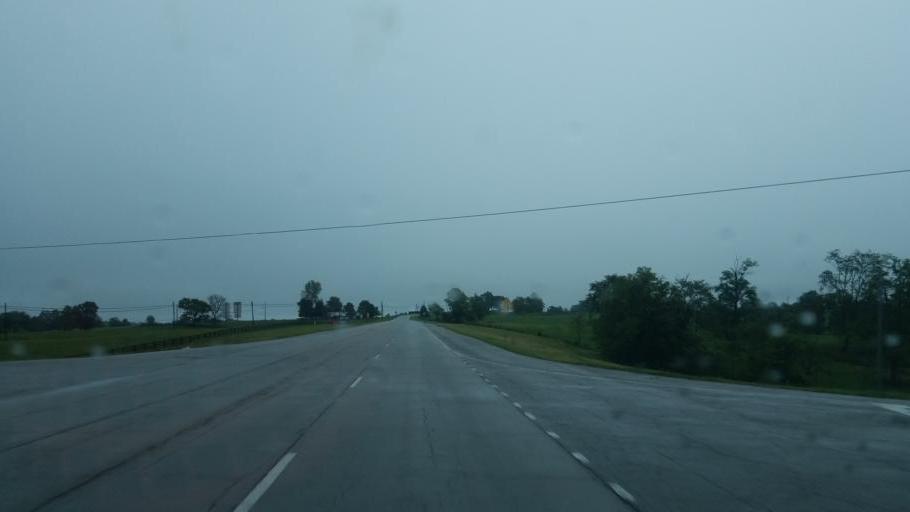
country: US
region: Kentucky
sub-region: Fleming County
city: Flemingsburg
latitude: 38.3960
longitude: -83.7059
